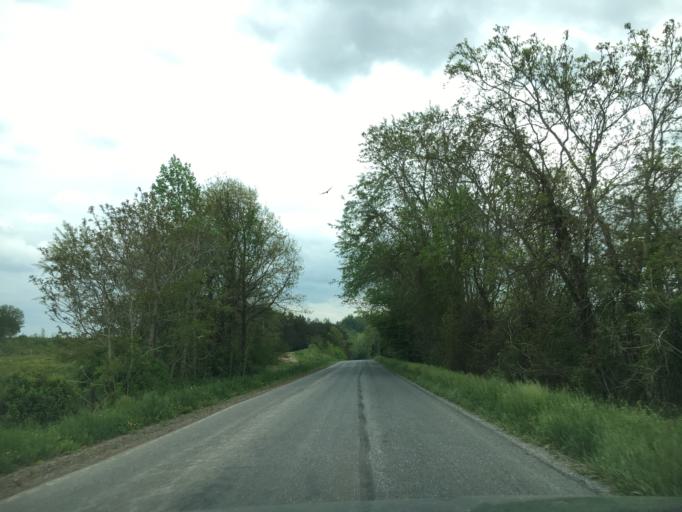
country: US
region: Virginia
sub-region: Campbell County
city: Rustburg
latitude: 37.1856
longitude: -79.0459
